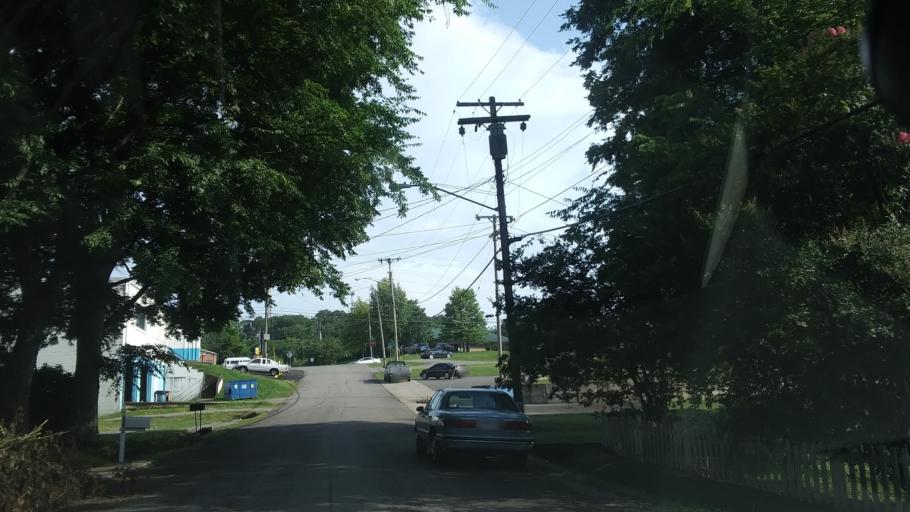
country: US
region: Tennessee
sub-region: Davidson County
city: Belle Meade
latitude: 36.1492
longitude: -86.8675
